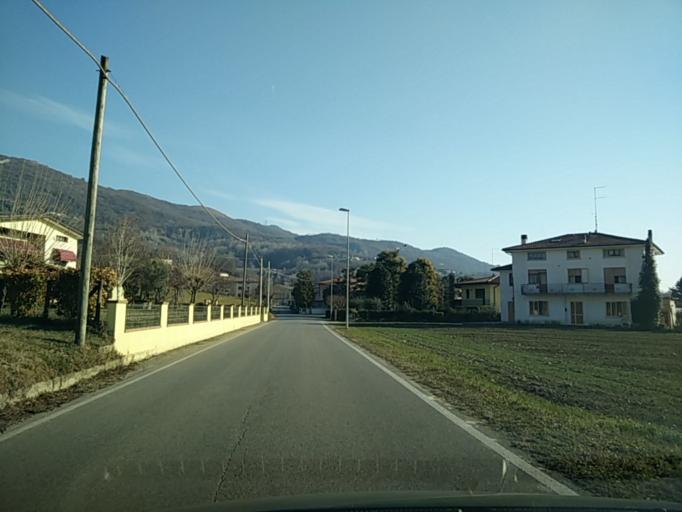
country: IT
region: Veneto
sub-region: Provincia di Treviso
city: Sarmede
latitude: 45.9760
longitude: 12.3920
